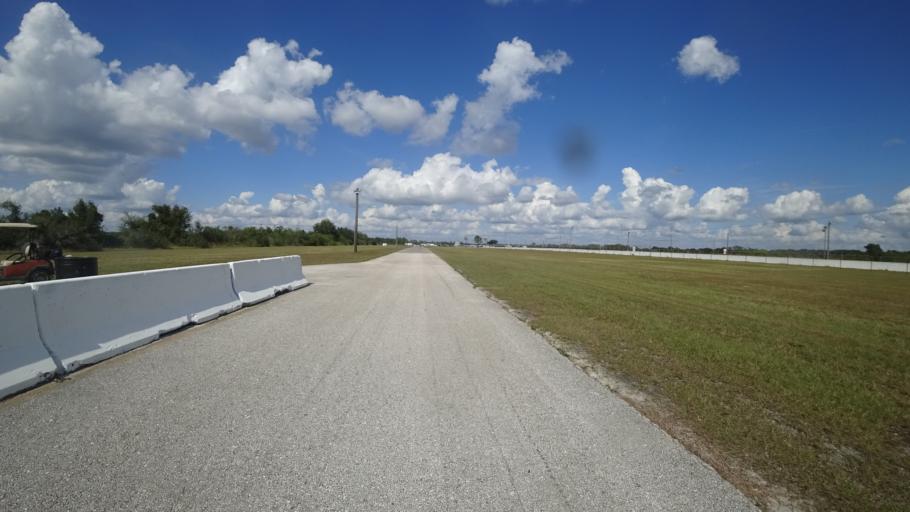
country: US
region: Florida
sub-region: Sarasota County
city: The Meadows
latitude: 27.4662
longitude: -82.3274
